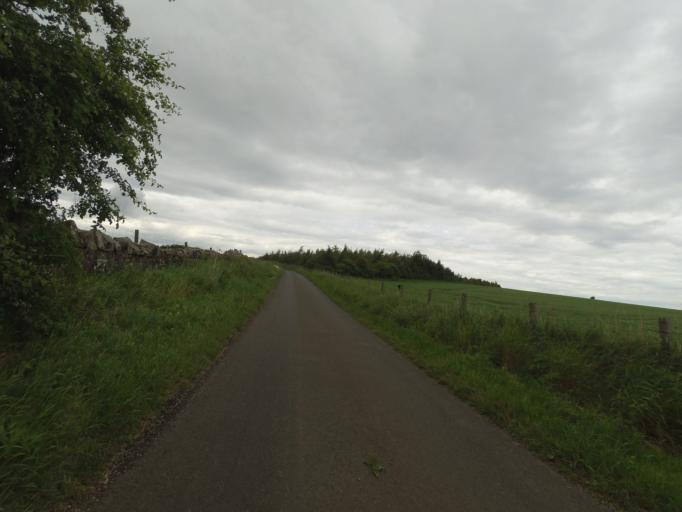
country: GB
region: Scotland
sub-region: East Lothian
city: Prestonpans
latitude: 55.9265
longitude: -2.9942
